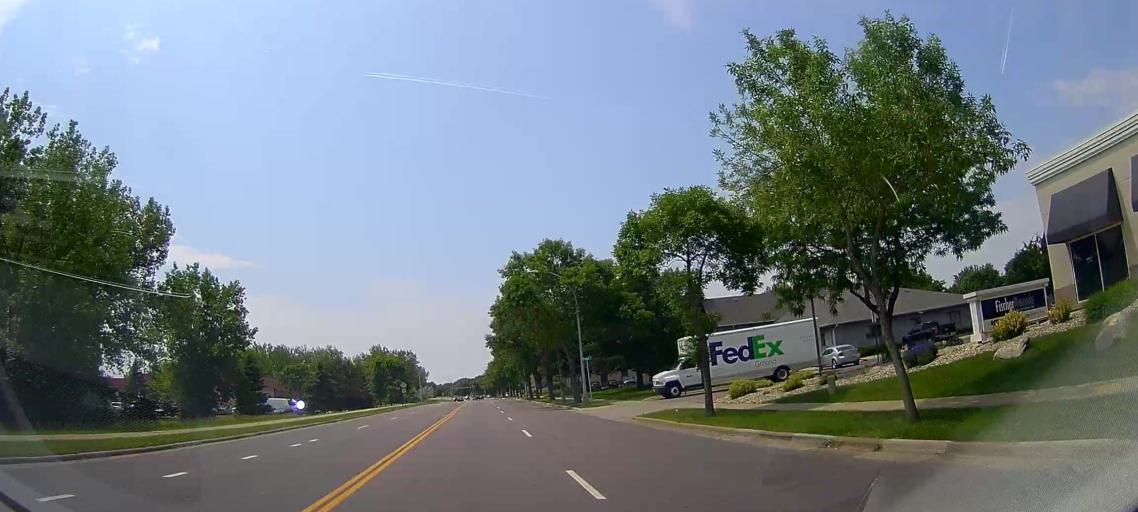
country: US
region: South Dakota
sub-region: Minnehaha County
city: Sioux Falls
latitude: 43.5084
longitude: -96.7540
